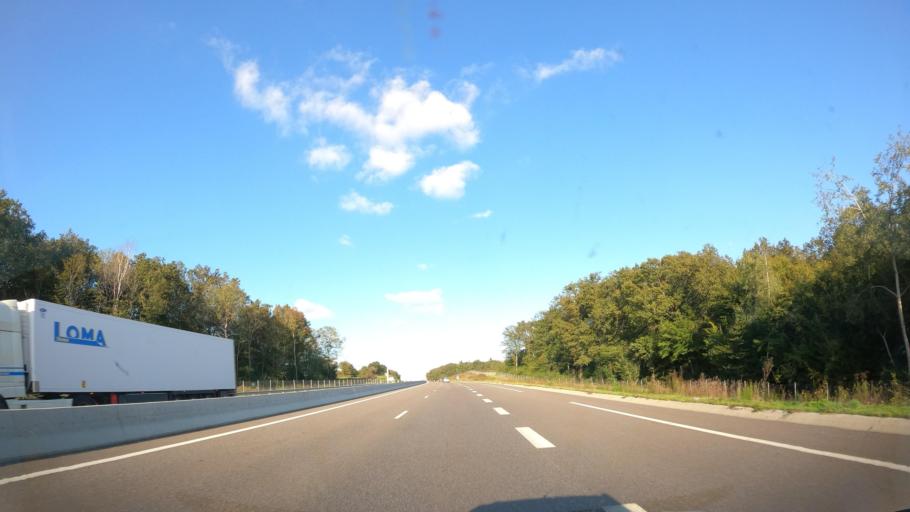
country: FR
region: Bourgogne
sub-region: Departement de Saone-et-Loire
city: Genelard
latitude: 46.5946
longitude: 4.2354
